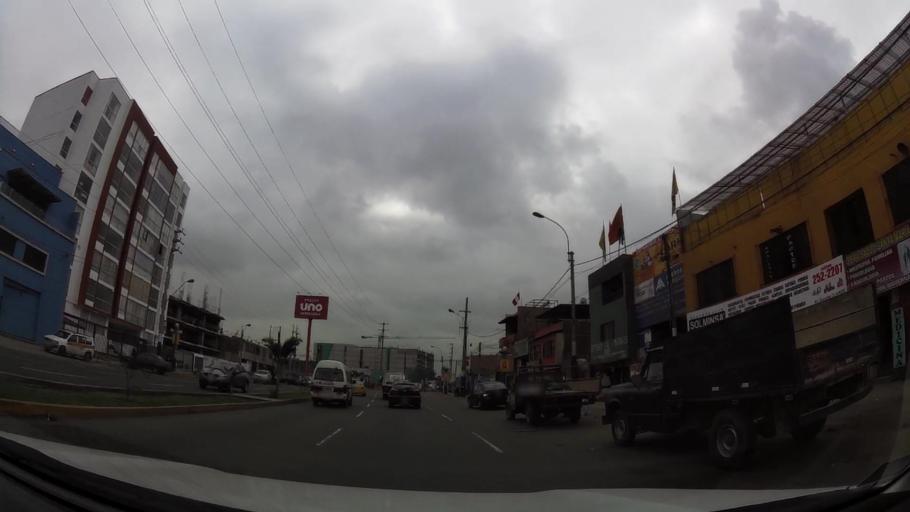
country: PE
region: Lima
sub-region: Lima
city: Surco
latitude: -12.1822
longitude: -76.9993
